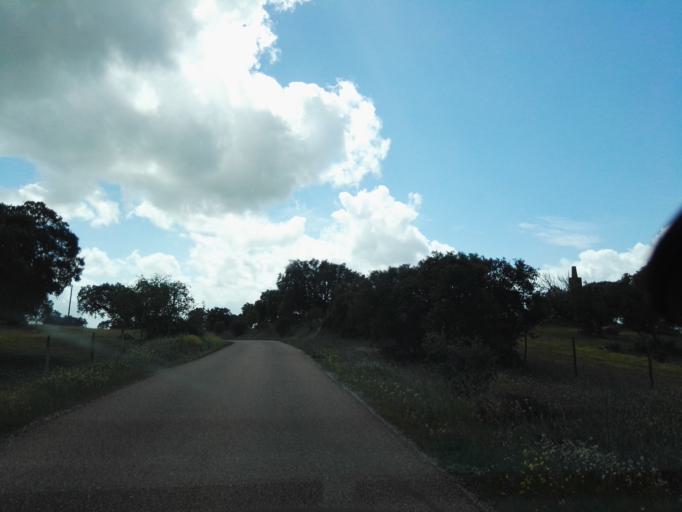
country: PT
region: Portalegre
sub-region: Elvas
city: Elvas
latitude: 38.9845
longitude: -7.1763
